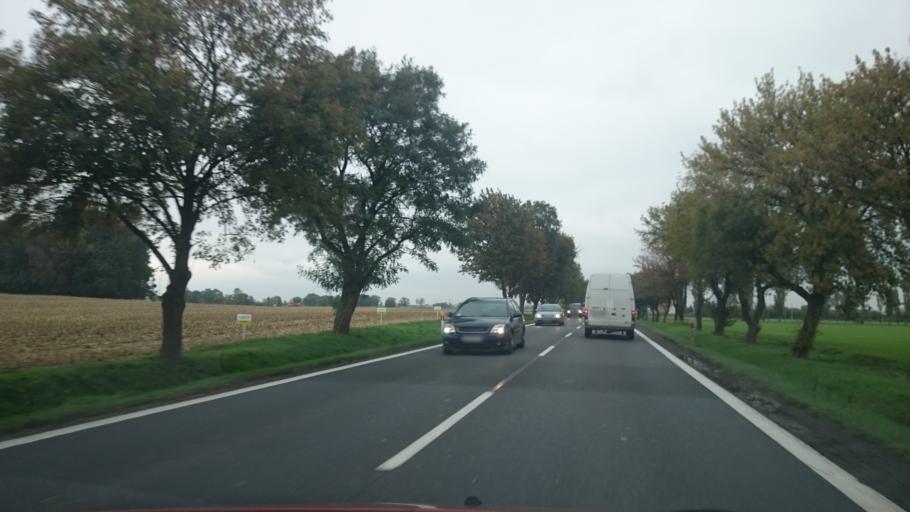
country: PL
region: Lower Silesian Voivodeship
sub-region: Powiat wroclawski
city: Kobierzyce
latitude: 50.9834
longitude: 16.9481
